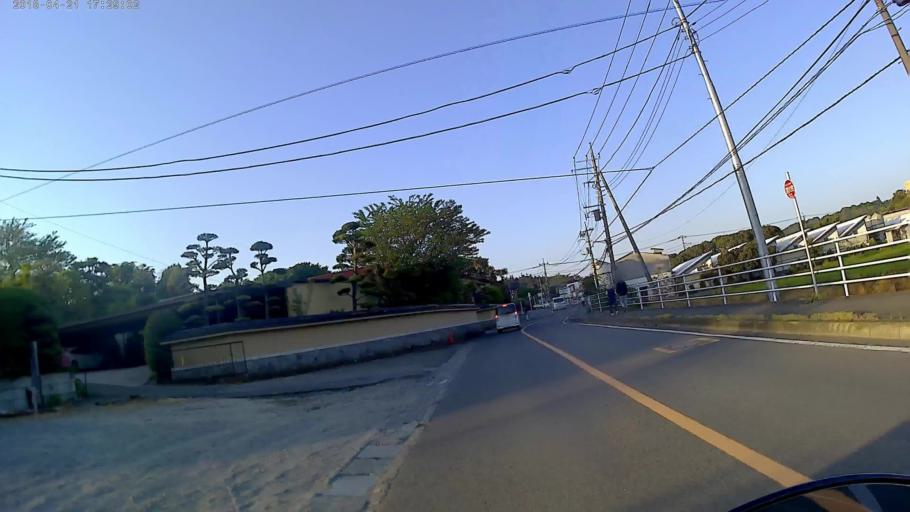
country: JP
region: Kanagawa
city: Atsugi
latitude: 35.4267
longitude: 139.4128
